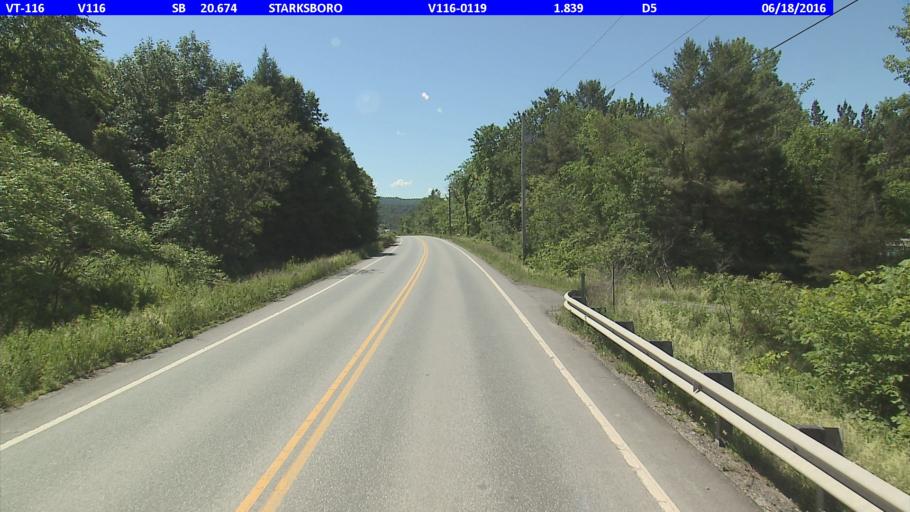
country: US
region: Vermont
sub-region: Addison County
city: Bristol
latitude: 44.2111
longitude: -73.0548
